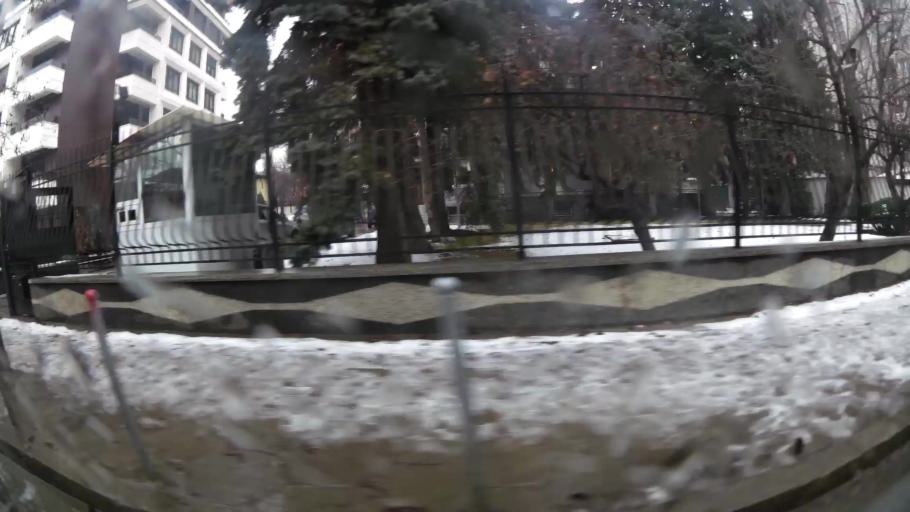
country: BG
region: Sofia-Capital
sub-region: Stolichna Obshtina
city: Sofia
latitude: 42.6748
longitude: 23.2849
